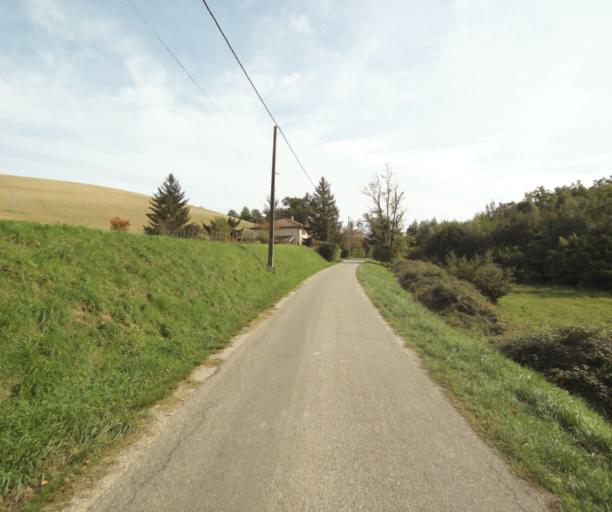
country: FR
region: Midi-Pyrenees
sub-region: Departement du Tarn-et-Garonne
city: Corbarieu
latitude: 43.9601
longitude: 1.3697
